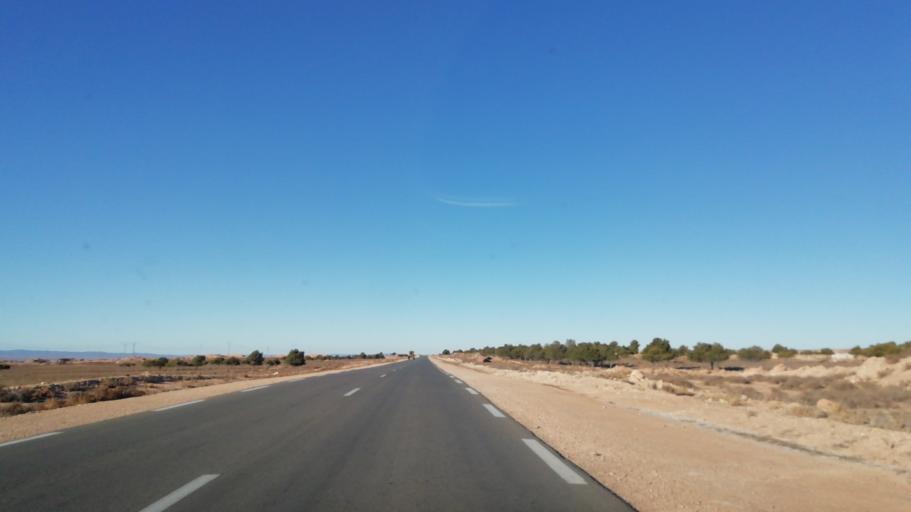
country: DZ
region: Tlemcen
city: Sebdou
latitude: 34.2719
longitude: -1.2585
